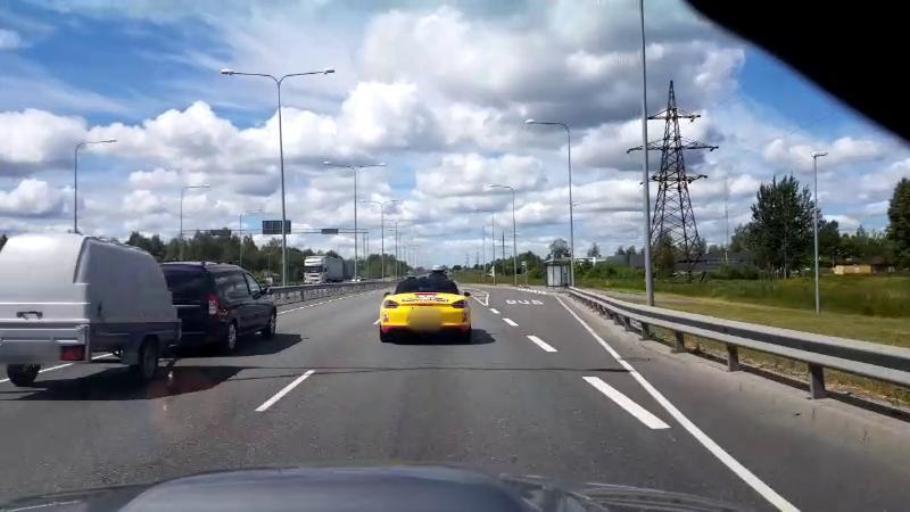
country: EE
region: Paernumaa
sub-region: Paernu linn
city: Parnu
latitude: 58.3939
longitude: 24.5337
